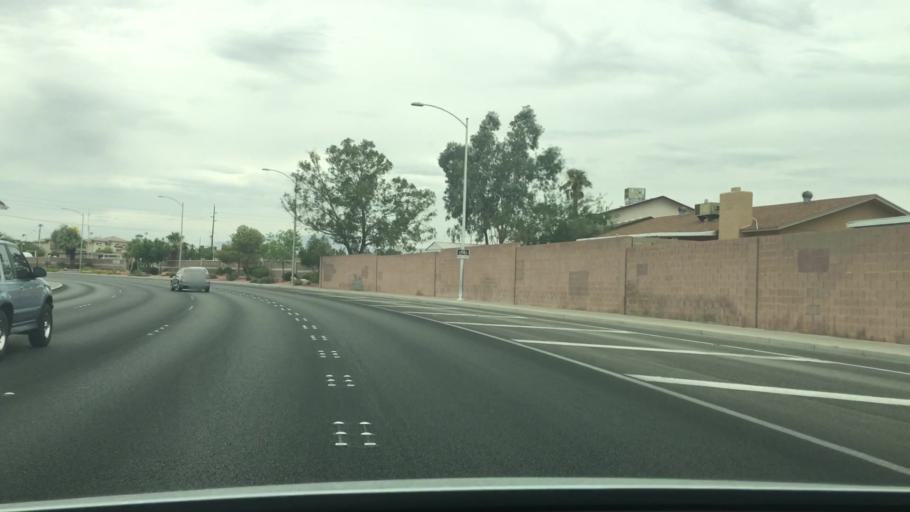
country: US
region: Nevada
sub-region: Clark County
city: Spring Valley
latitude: 36.1612
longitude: -115.2617
